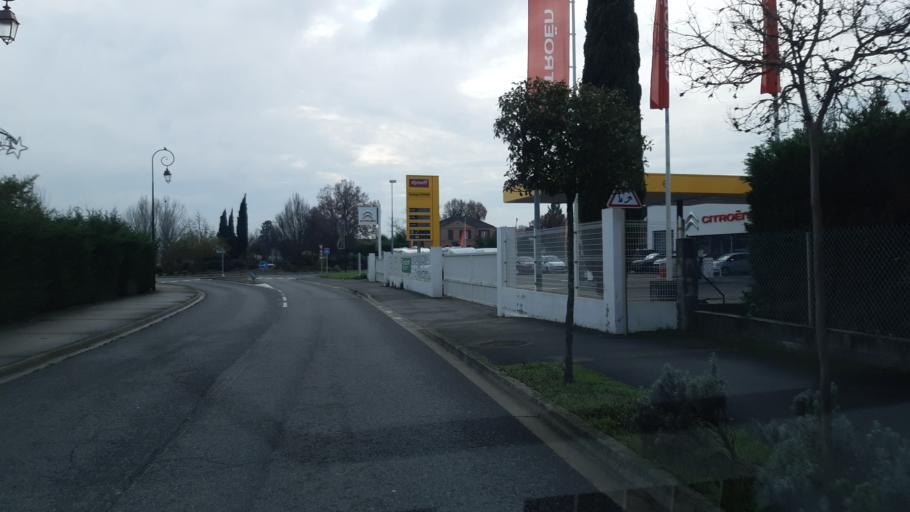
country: FR
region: Midi-Pyrenees
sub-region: Departement de la Haute-Garonne
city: Pibrac
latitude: 43.6111
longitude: 1.2848
